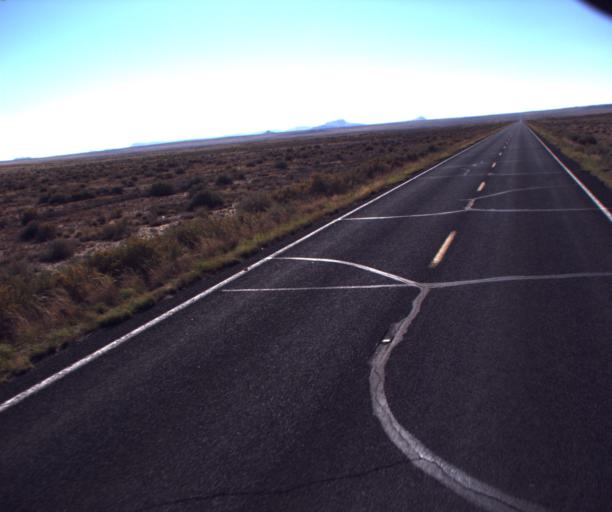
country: US
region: Arizona
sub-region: Navajo County
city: First Mesa
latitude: 35.7055
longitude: -110.5094
